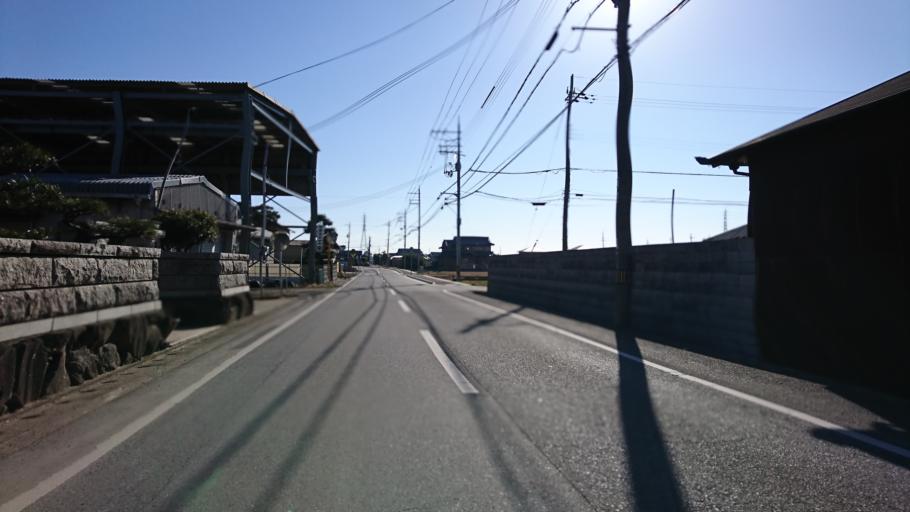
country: JP
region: Hyogo
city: Miki
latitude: 34.7476
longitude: 134.9327
